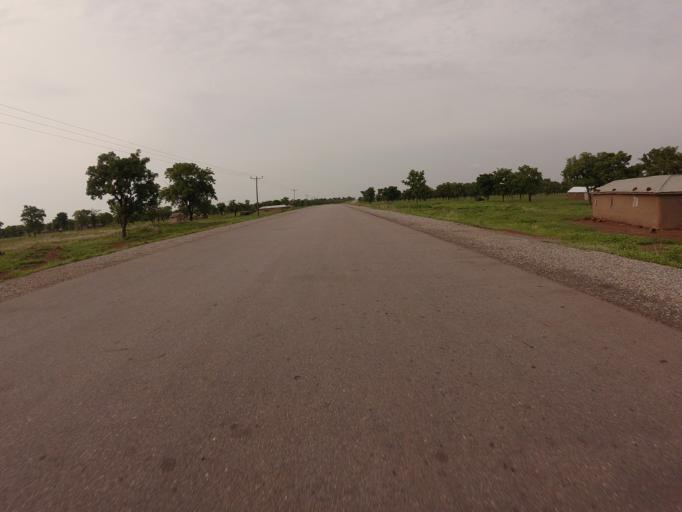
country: GH
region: Northern
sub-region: Yendi
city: Yendi
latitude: 9.8240
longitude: -0.1198
